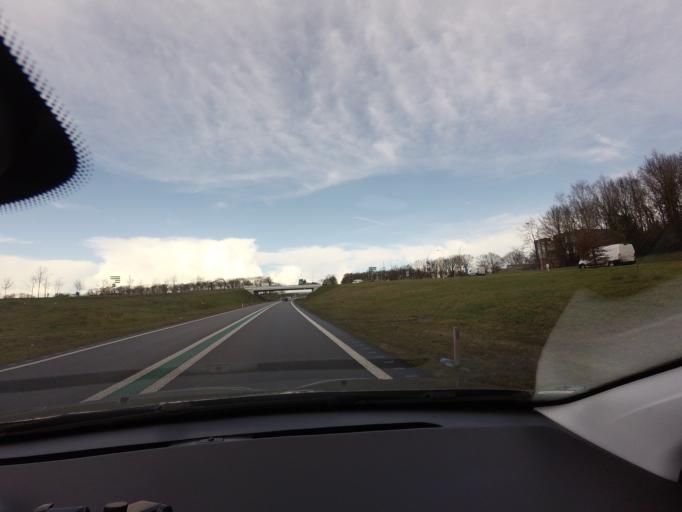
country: NL
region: Drenthe
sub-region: Gemeente Borger-Odoorn
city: Borger
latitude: 52.9221
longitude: 6.7857
